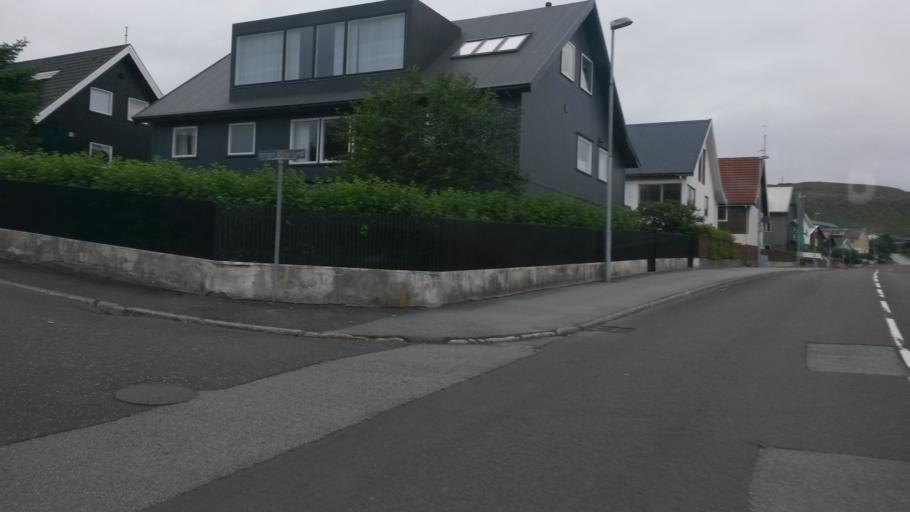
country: FO
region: Streymoy
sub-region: Torshavn
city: Torshavn
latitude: 62.0181
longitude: -6.7805
